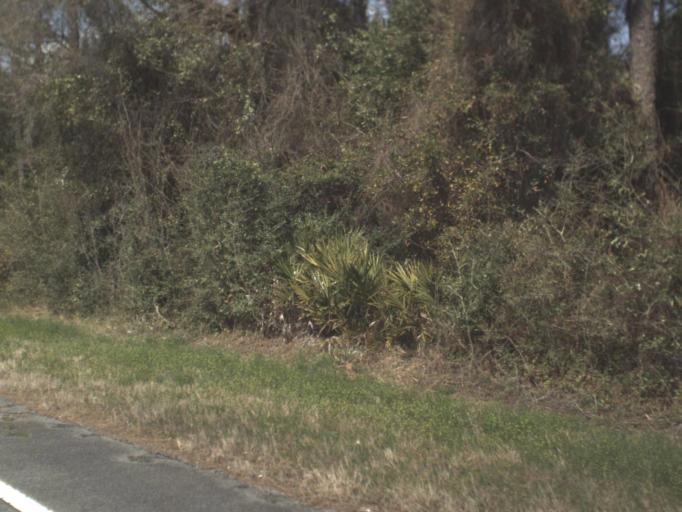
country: US
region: Florida
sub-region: Franklin County
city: Carrabelle
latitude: 29.9524
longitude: -84.5042
